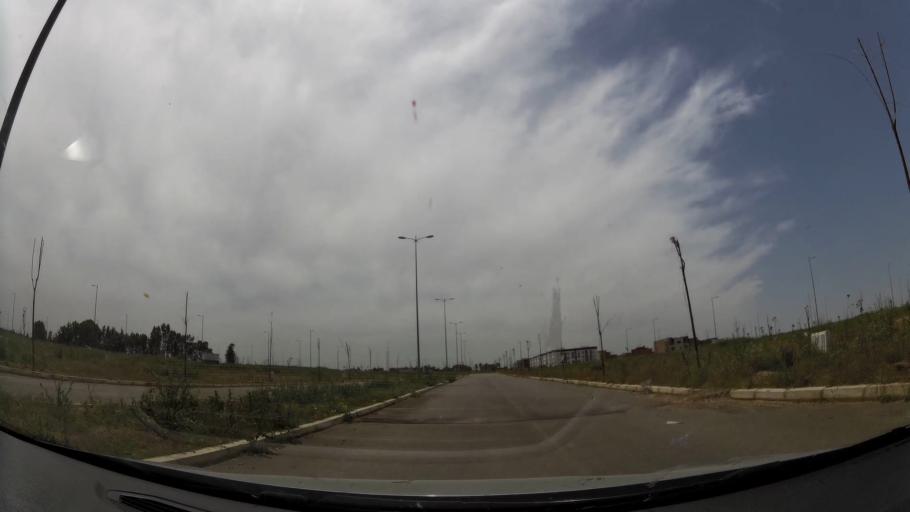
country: MA
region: Rabat-Sale-Zemmour-Zaer
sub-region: Khemisset
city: Khemisset
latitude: 33.8170
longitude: -6.0859
